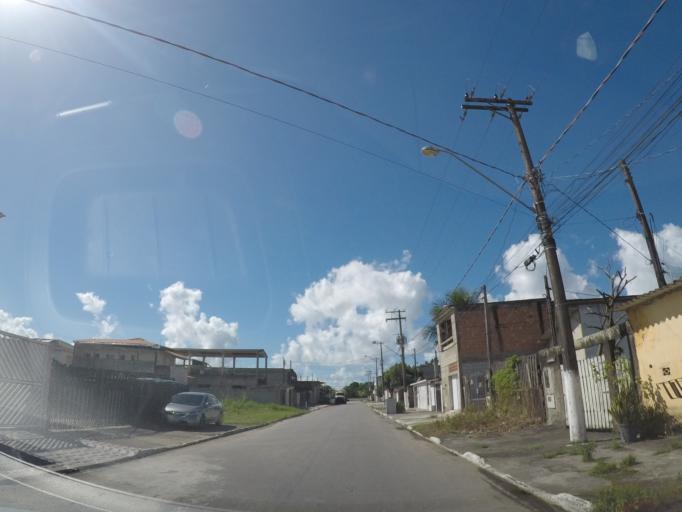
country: BR
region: Sao Paulo
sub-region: Praia Grande
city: Praia Grande
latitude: -24.0237
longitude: -46.5074
